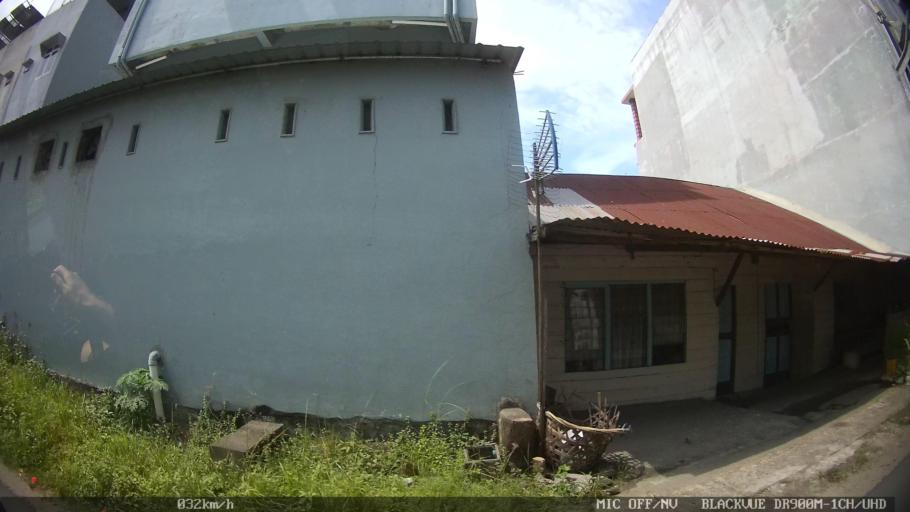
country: ID
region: North Sumatra
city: Labuhan Deli
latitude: 3.6885
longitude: 98.6609
